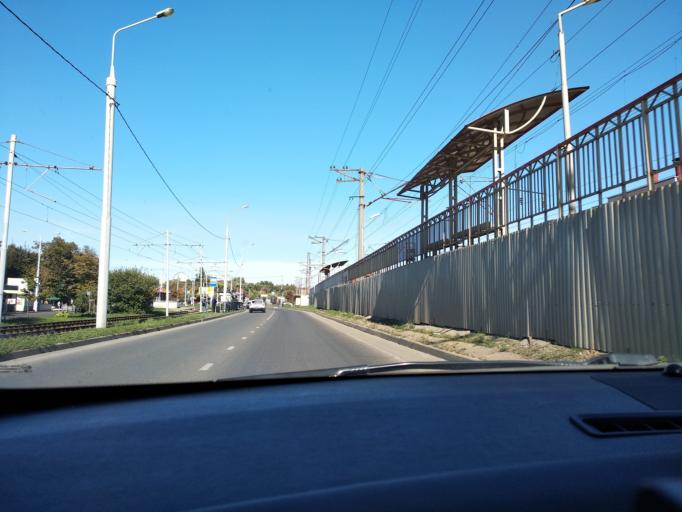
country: RU
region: Adygeya
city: Yablonovskiy
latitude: 45.0050
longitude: 38.9667
